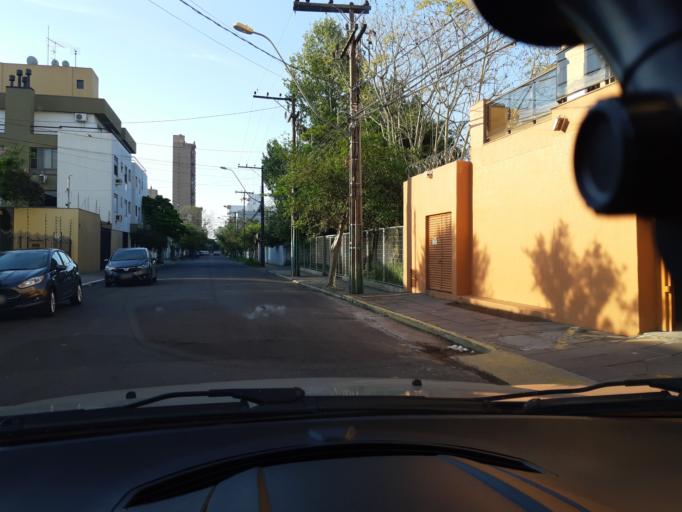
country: BR
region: Rio Grande do Sul
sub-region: Sao Leopoldo
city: Sao Leopoldo
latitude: -29.7671
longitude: -51.1413
